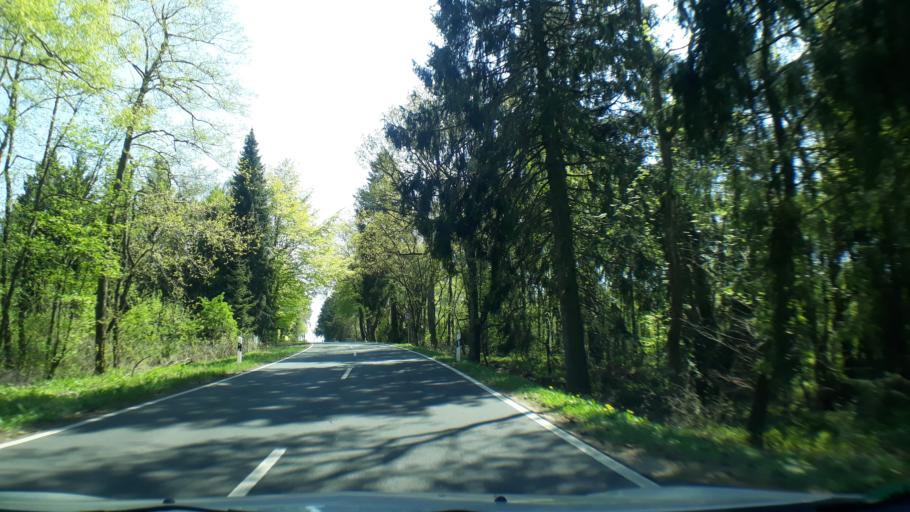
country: DE
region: North Rhine-Westphalia
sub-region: Regierungsbezirk Koln
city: Simmerath
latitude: 50.6443
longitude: 6.2637
